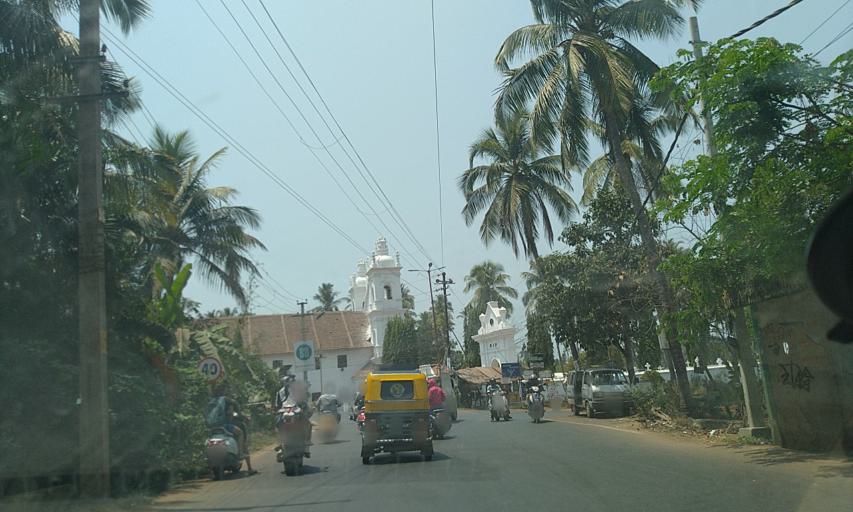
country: IN
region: Goa
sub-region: North Goa
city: Vagator
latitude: 15.5900
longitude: 73.7650
